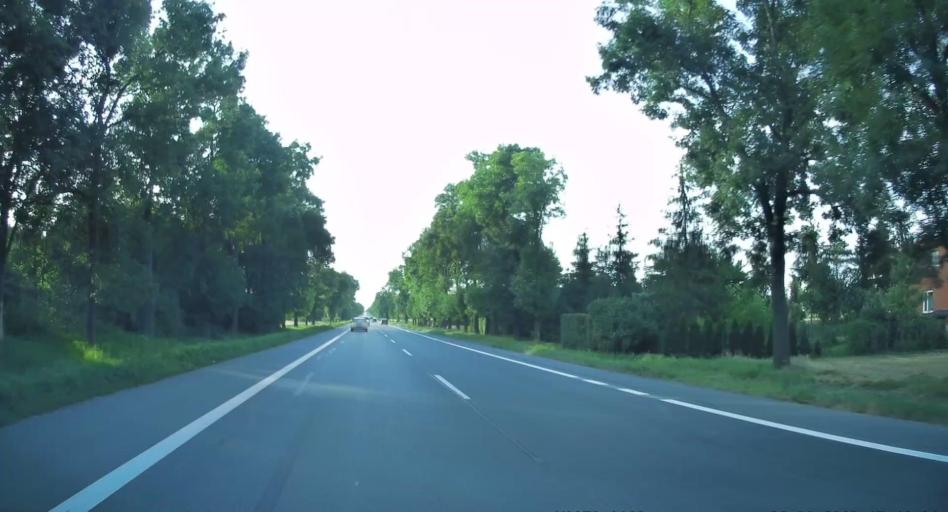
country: PL
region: Lesser Poland Voivodeship
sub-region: Powiat krakowski
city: Slomniki
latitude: 50.2566
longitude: 20.0841
